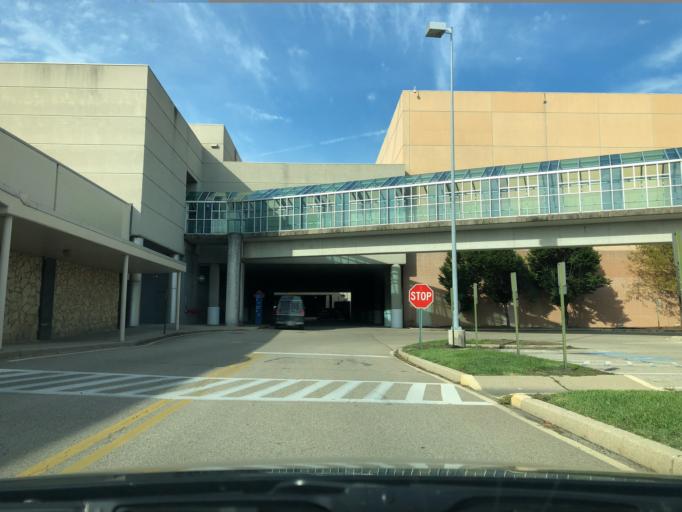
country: US
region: Ohio
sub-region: Hamilton County
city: Glendale
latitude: 39.2896
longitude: -84.4625
